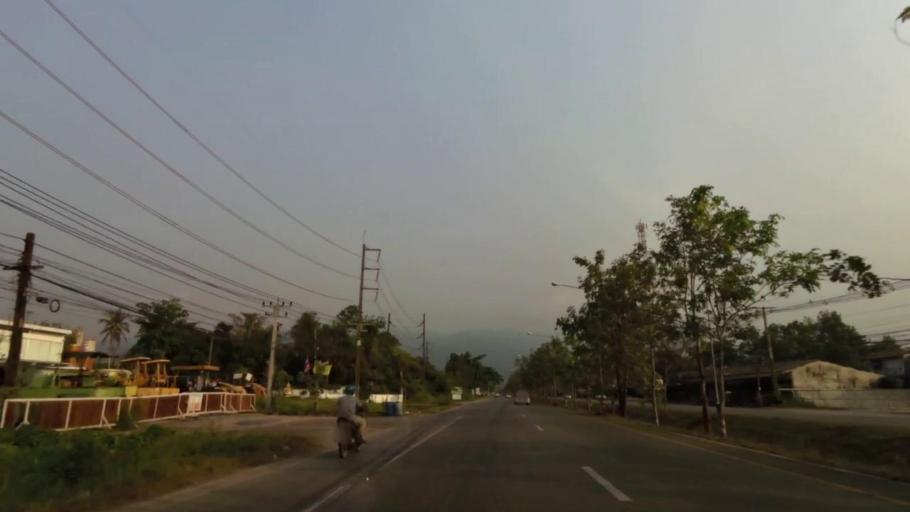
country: TH
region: Chanthaburi
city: Chanthaburi
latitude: 12.5955
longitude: 102.1440
